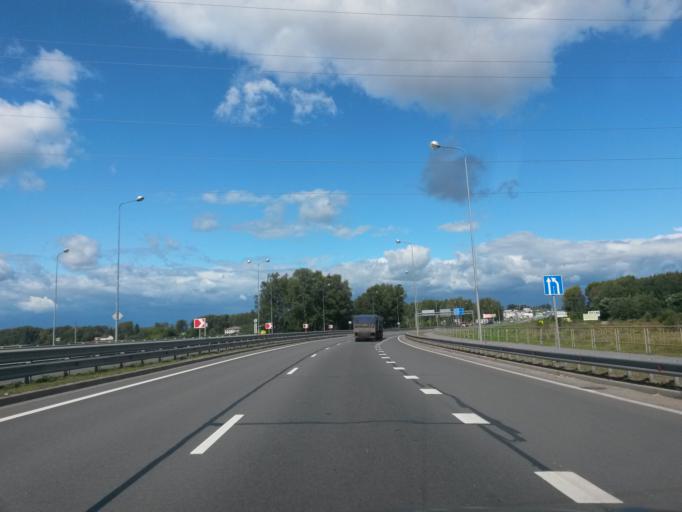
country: RU
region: Jaroslavl
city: Yaroslavl
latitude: 57.6899
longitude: 39.8992
